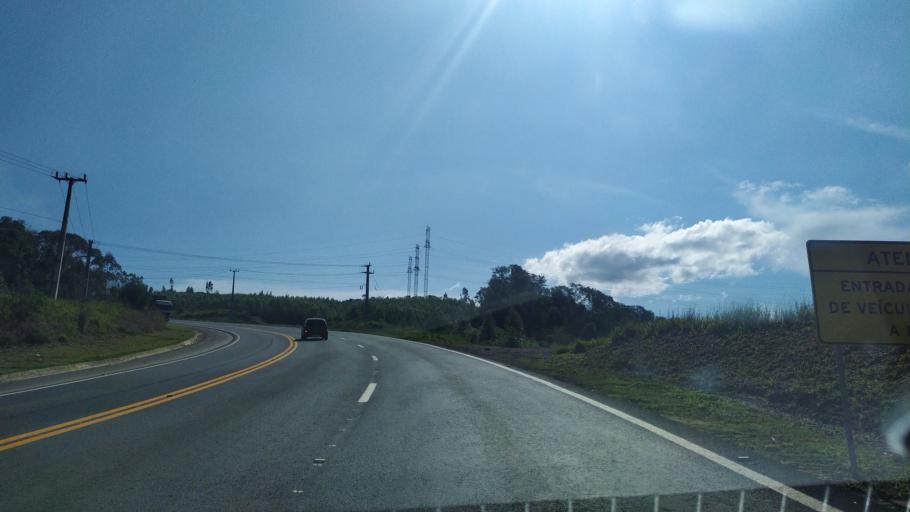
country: BR
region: Parana
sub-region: Telemaco Borba
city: Telemaco Borba
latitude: -24.2571
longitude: -50.7276
